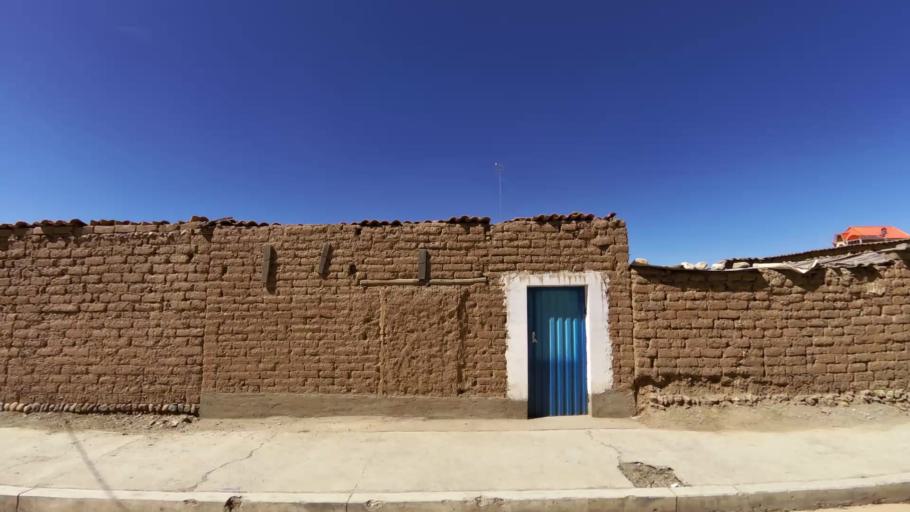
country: BO
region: La Paz
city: La Paz
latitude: -16.5329
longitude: -68.2088
